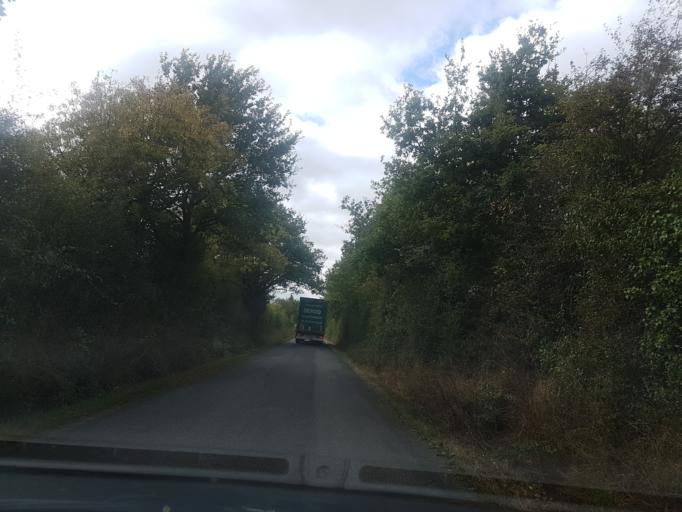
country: FR
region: Pays de la Loire
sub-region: Departement de la Loire-Atlantique
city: Saint-Mars-du-Desert
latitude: 47.3939
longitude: -1.4081
